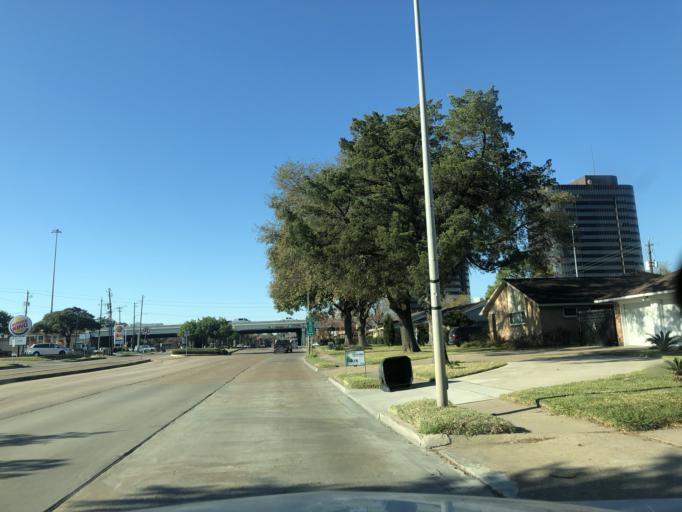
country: US
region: Texas
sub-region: Harris County
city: Bellaire
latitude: 29.6991
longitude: -95.5162
